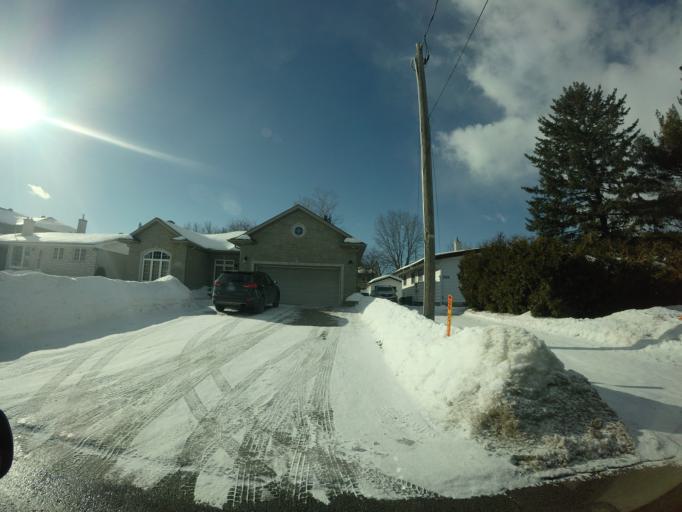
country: CA
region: Ontario
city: Ottawa
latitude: 45.4219
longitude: -75.6076
